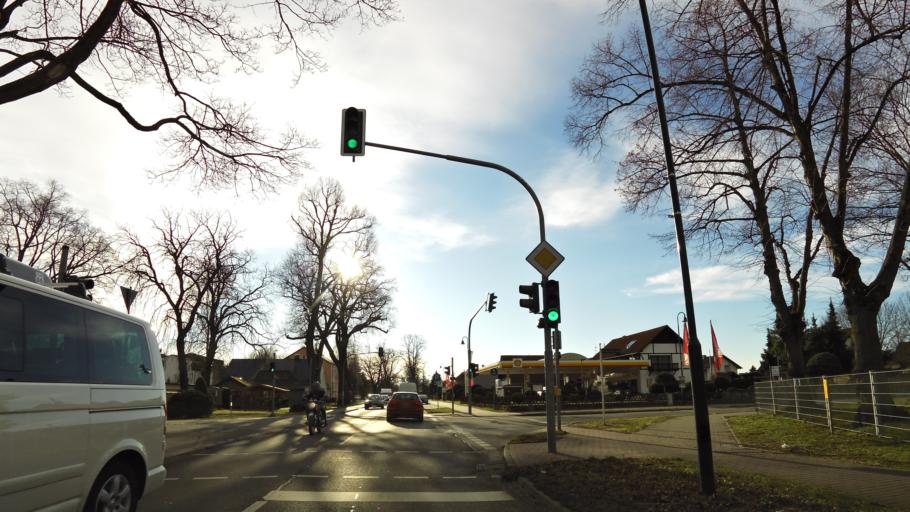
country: DE
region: Brandenburg
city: Petershagen
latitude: 52.5144
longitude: 13.7465
